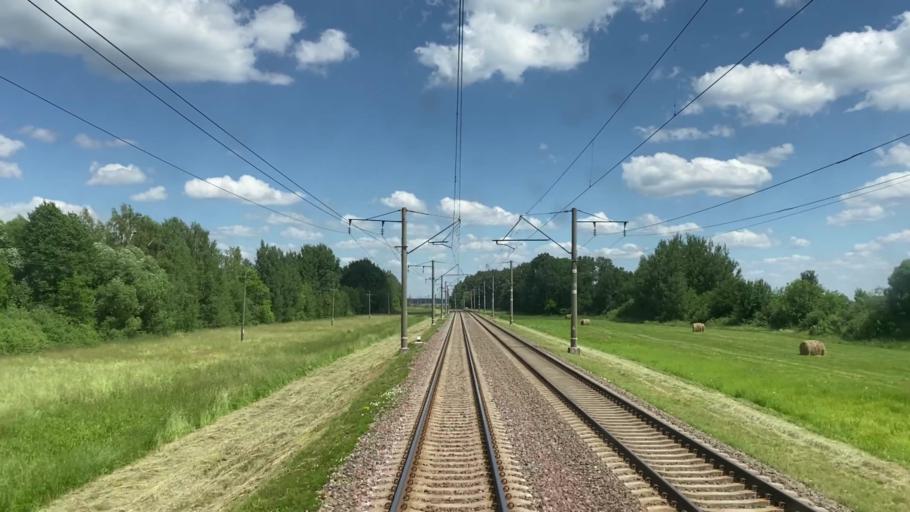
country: BY
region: Brest
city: Ivatsevichy
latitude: 52.7577
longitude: 25.3931
